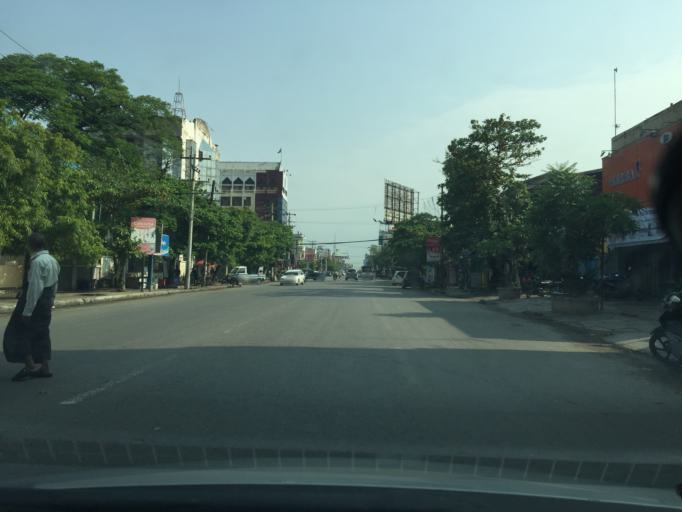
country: MM
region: Mandalay
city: Mandalay
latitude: 21.9701
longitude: 96.0837
